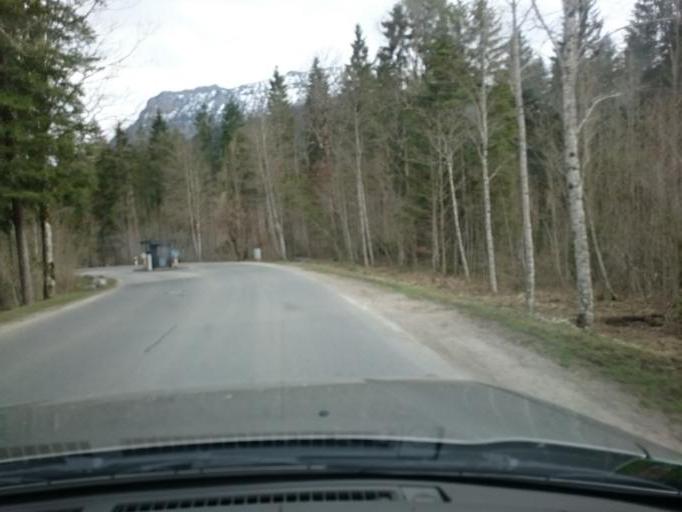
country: DE
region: Bavaria
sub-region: Upper Bavaria
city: Unterammergau
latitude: 47.5689
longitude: 10.9574
